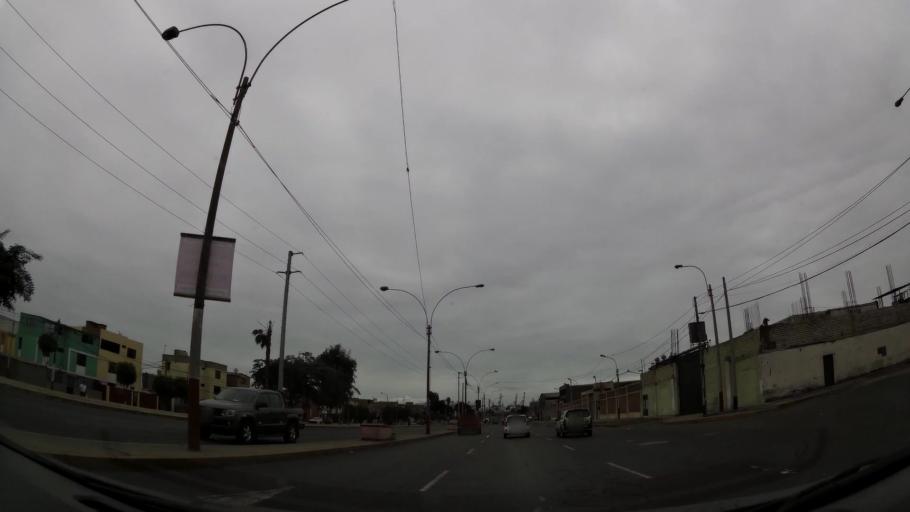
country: PE
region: Callao
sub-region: Callao
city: Callao
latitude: -12.0510
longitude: -77.1281
